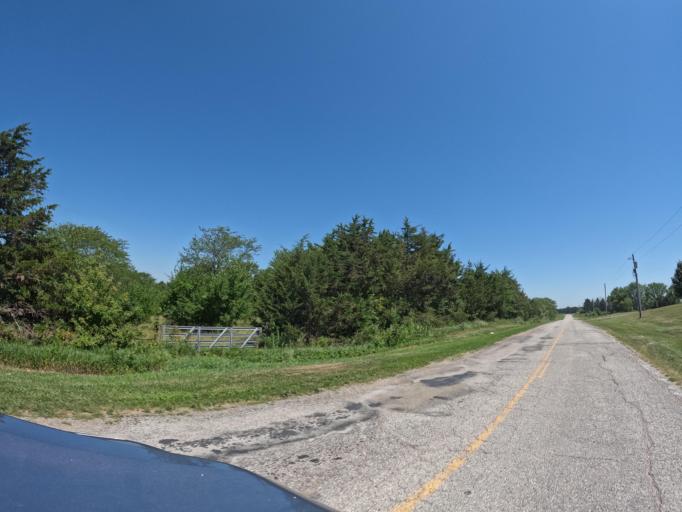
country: US
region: Iowa
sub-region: Monroe County
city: Albia
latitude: 41.0279
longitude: -92.7713
